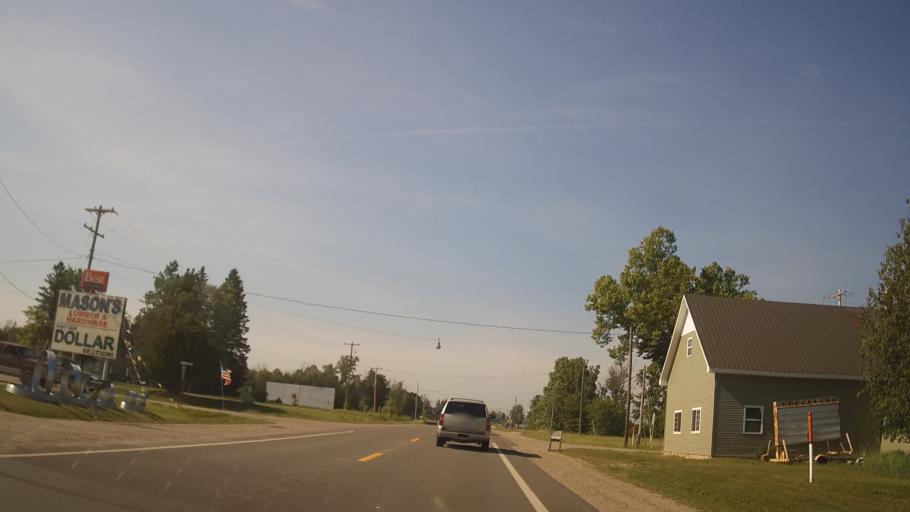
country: US
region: Michigan
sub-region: Ogemaw County
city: West Branch
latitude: 44.4064
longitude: -84.1163
